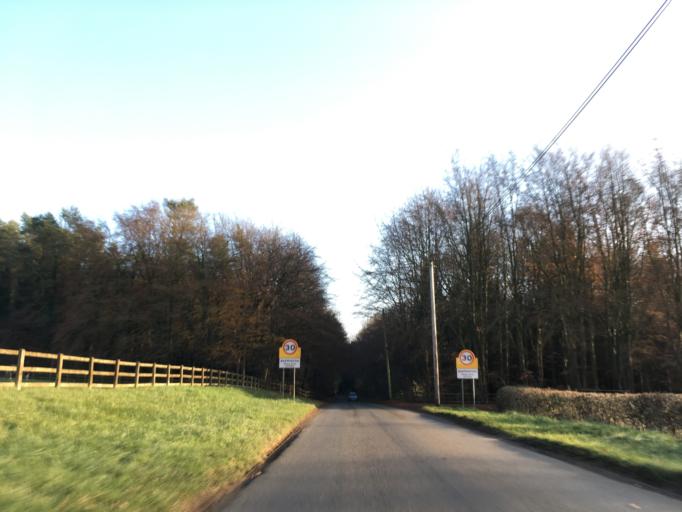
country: GB
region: England
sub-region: Wiltshire
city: Luckington
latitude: 51.5451
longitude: -2.2917
